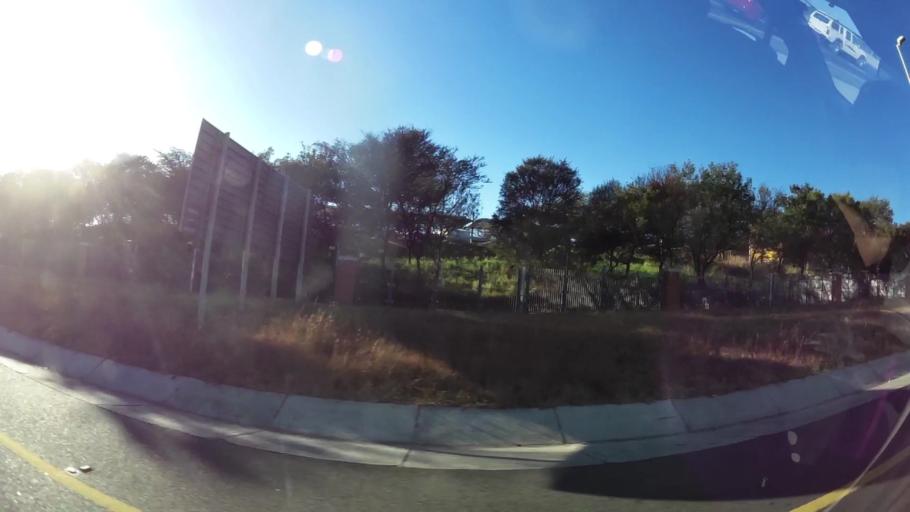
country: ZA
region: Gauteng
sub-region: City of Johannesburg Metropolitan Municipality
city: Roodepoort
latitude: -26.1495
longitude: 27.9287
